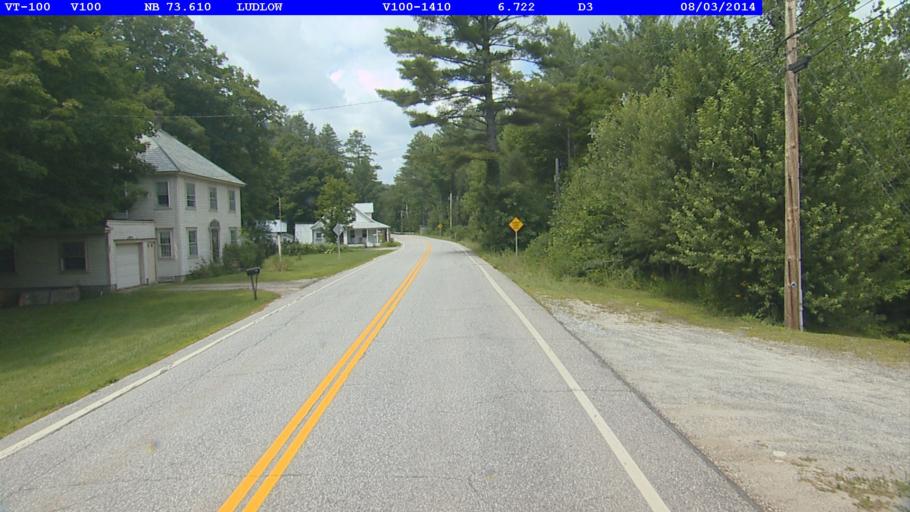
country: US
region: Vermont
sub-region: Windsor County
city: Chester
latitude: 43.4420
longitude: -72.6993
